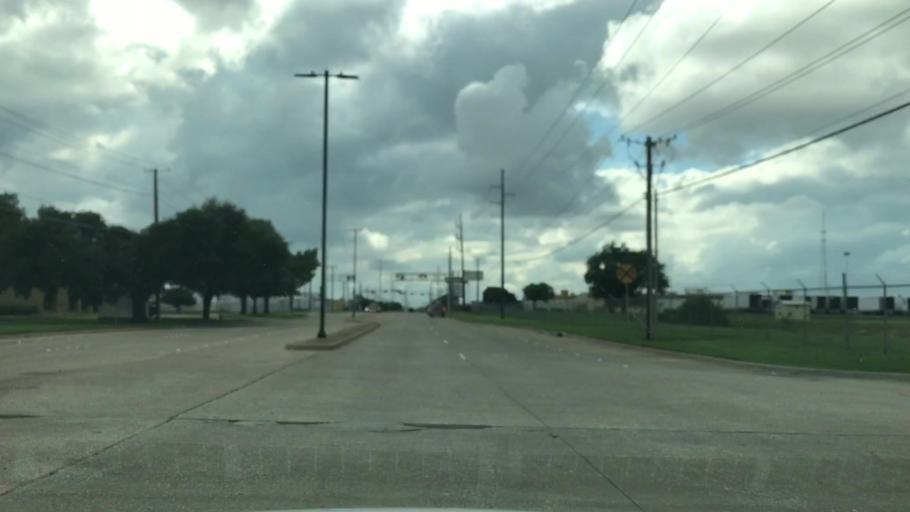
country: US
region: Texas
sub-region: Dallas County
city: Garland
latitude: 32.8945
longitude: -96.6704
